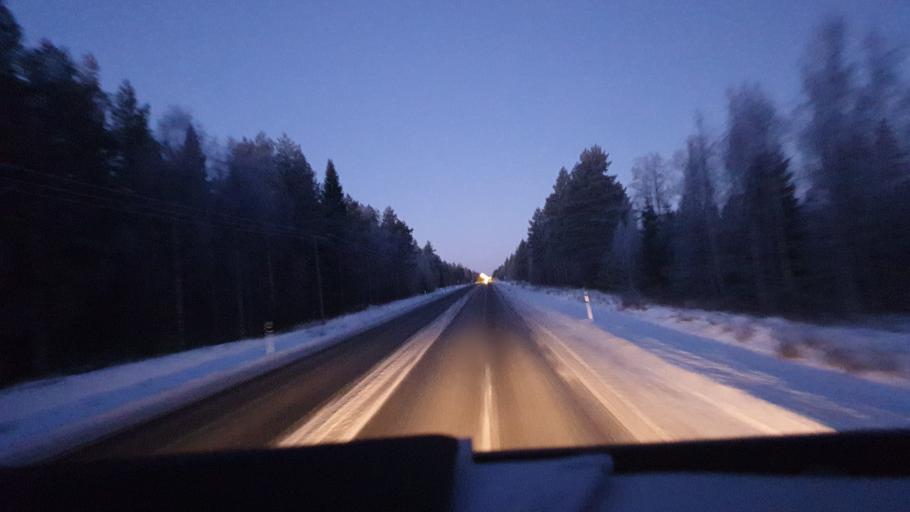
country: FI
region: Northern Ostrobothnia
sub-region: Raahe
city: Siikajoki
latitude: 64.6929
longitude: 24.6654
